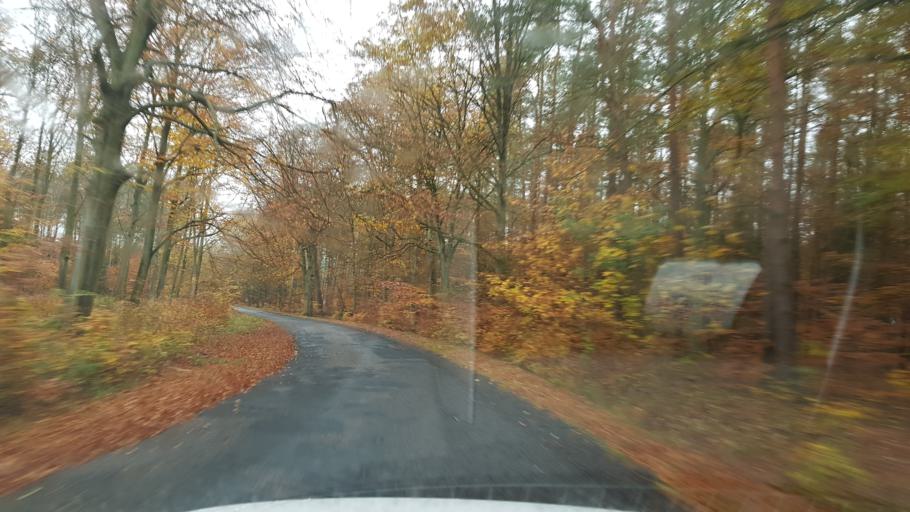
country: PL
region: West Pomeranian Voivodeship
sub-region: Powiat goleniowski
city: Stepnica
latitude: 53.6581
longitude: 14.6905
